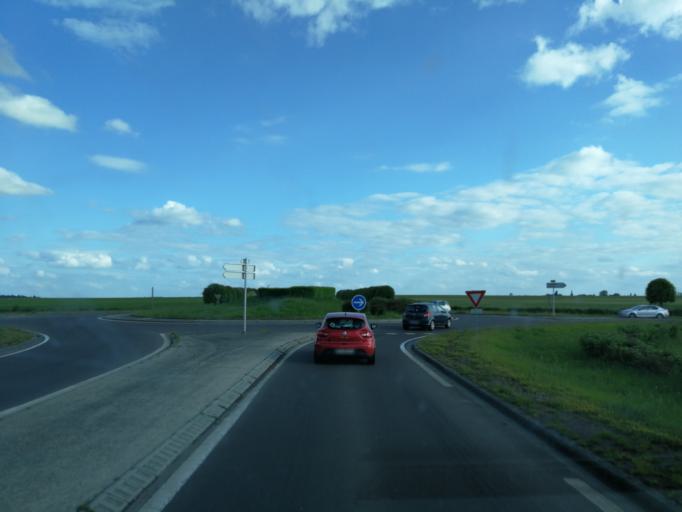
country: FR
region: Haute-Normandie
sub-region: Departement de l'Eure
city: Le Neubourg
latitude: 49.0754
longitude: 0.9210
